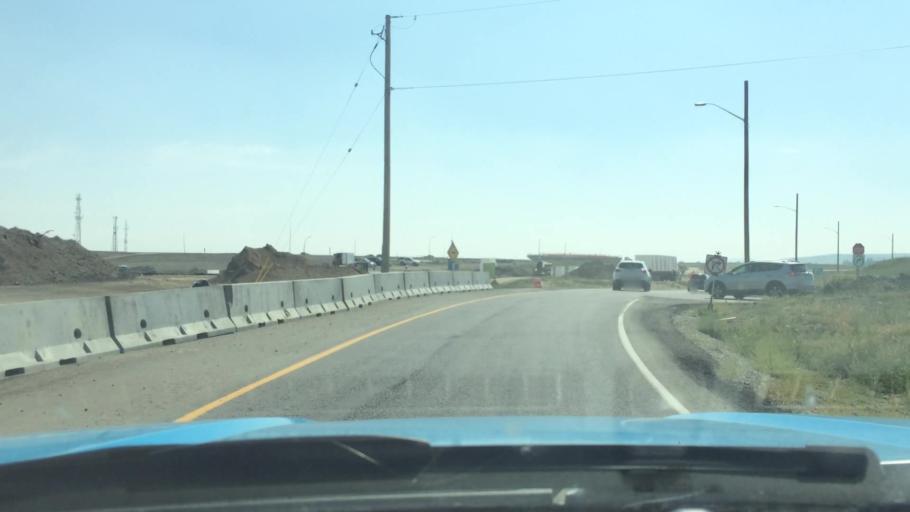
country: CA
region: Alberta
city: Calgary
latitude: 50.8961
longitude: -114.0576
